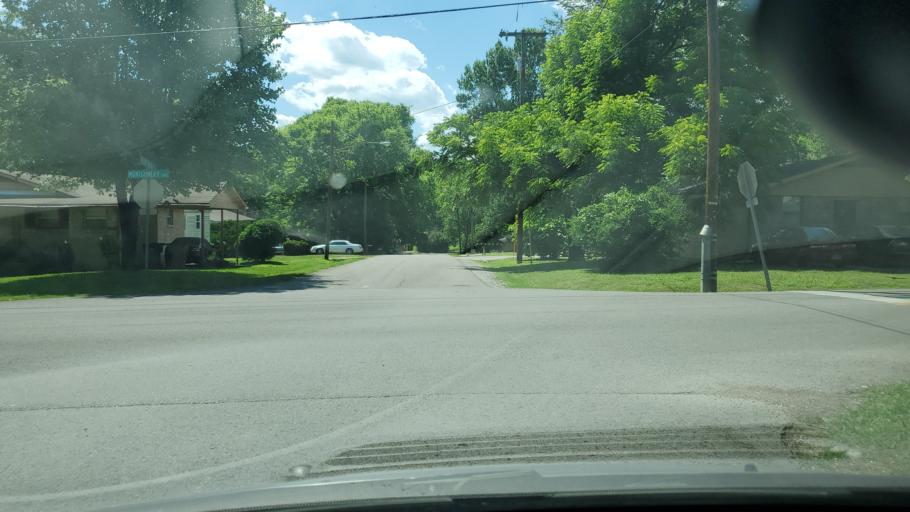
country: US
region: Tennessee
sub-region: Davidson County
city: Nashville
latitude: 36.1971
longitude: -86.7552
